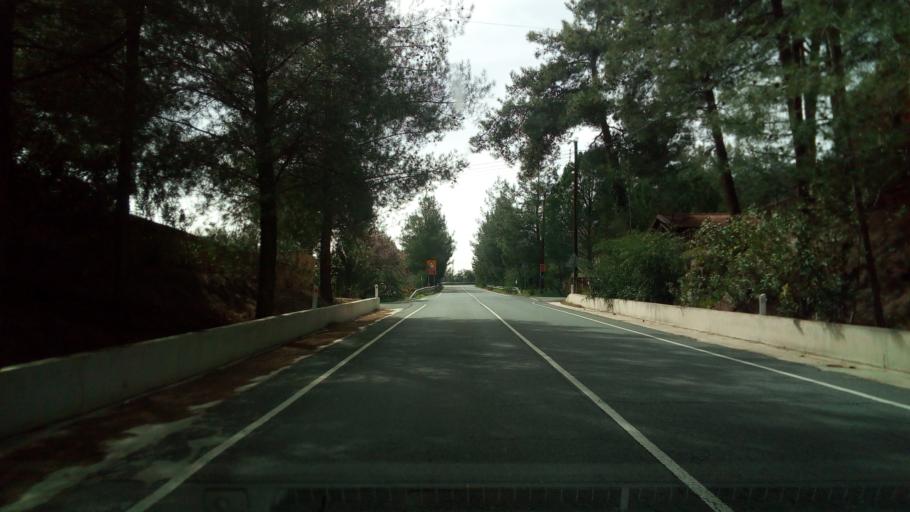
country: CY
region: Limassol
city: Pelendri
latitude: 34.8606
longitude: 32.9095
